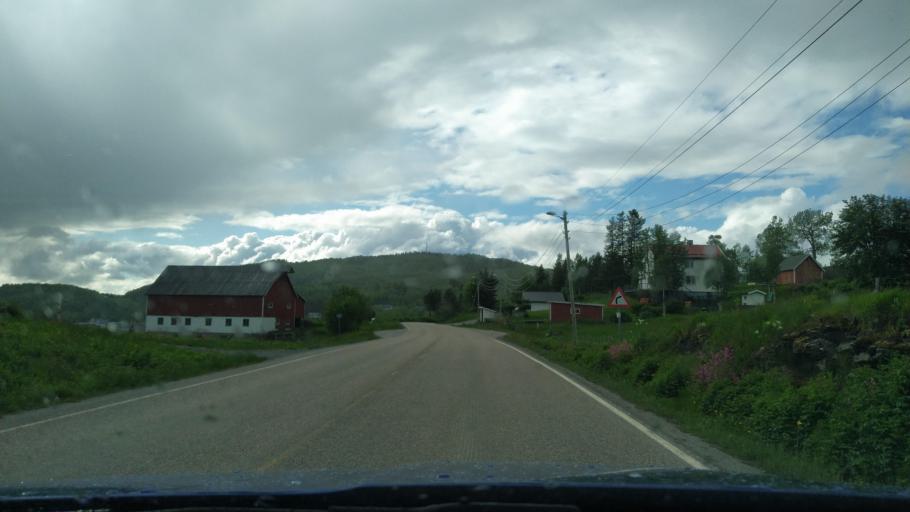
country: NO
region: Troms
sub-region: Sorreisa
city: Sorreisa
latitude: 69.1612
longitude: 18.1220
